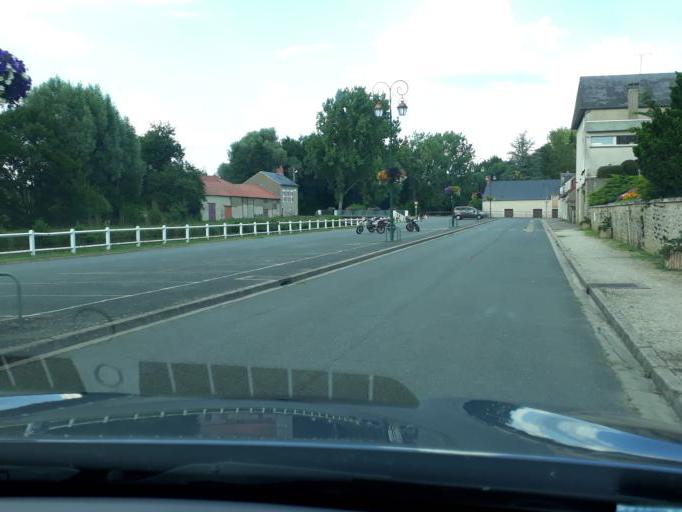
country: FR
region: Centre
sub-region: Departement du Cher
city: Jouet-sur-l'Aubois
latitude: 46.9511
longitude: 2.9444
